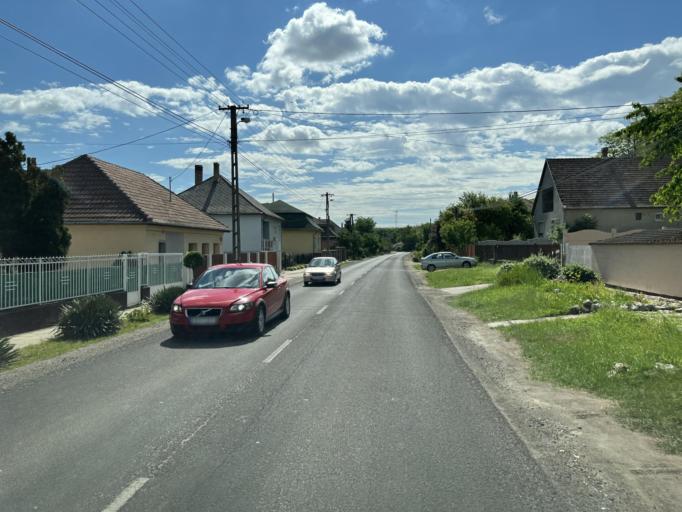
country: HU
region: Pest
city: Valko
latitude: 47.5638
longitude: 19.4998
